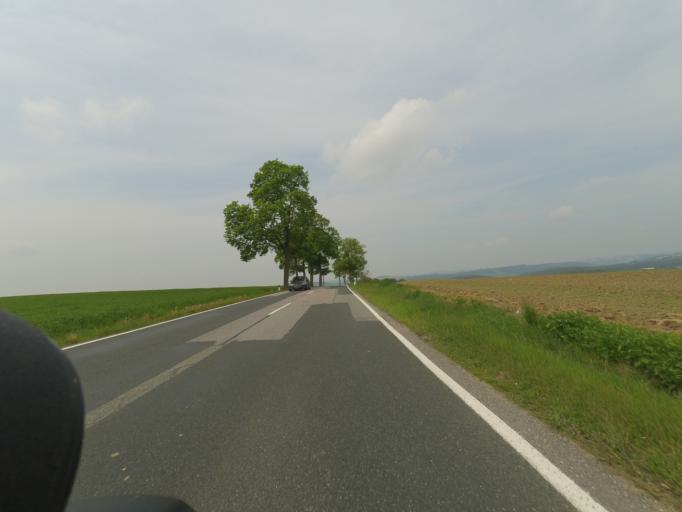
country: DE
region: Saxony
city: Wolkenstein
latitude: 50.6482
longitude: 13.0892
